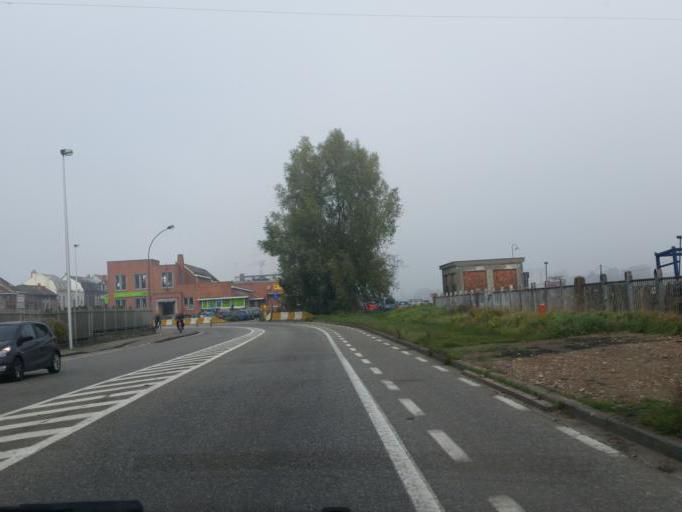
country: BE
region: Flanders
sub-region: Provincie Oost-Vlaanderen
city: Gent
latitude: 51.0608
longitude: 3.7365
